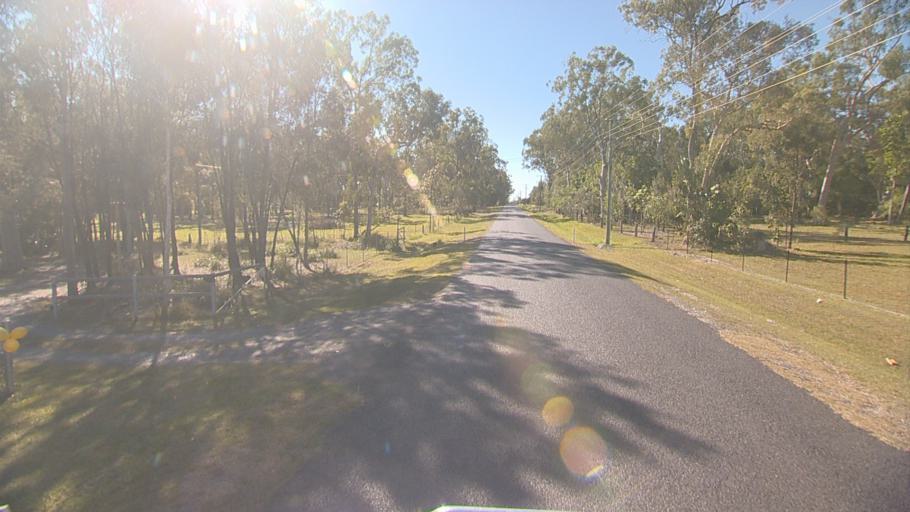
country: AU
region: Queensland
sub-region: Logan
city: Logan Reserve
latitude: -27.7287
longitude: 153.0726
